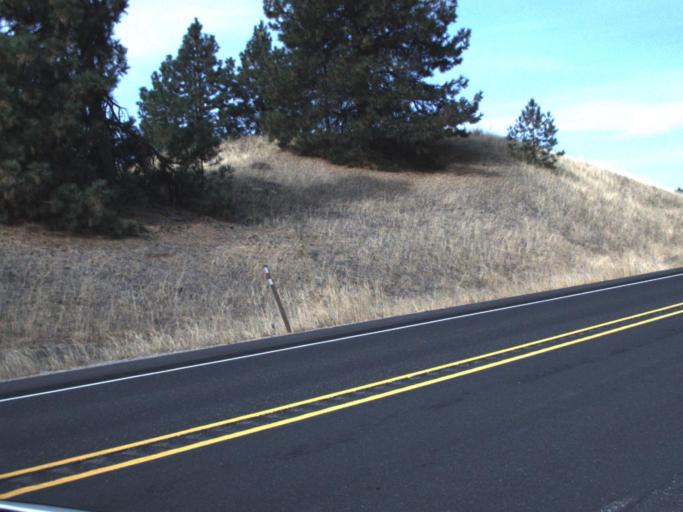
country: US
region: Washington
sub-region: Spokane County
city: Deer Park
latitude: 47.8982
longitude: -117.4345
